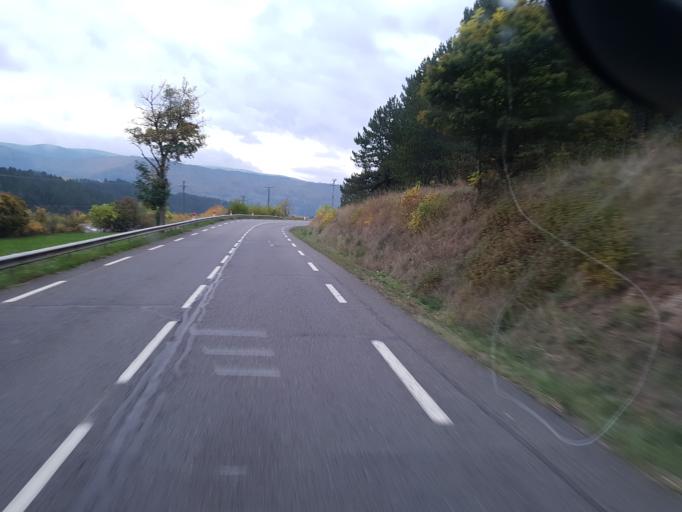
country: FR
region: Languedoc-Roussillon
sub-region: Departement de la Lozere
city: Mende
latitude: 44.5416
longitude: 3.6115
